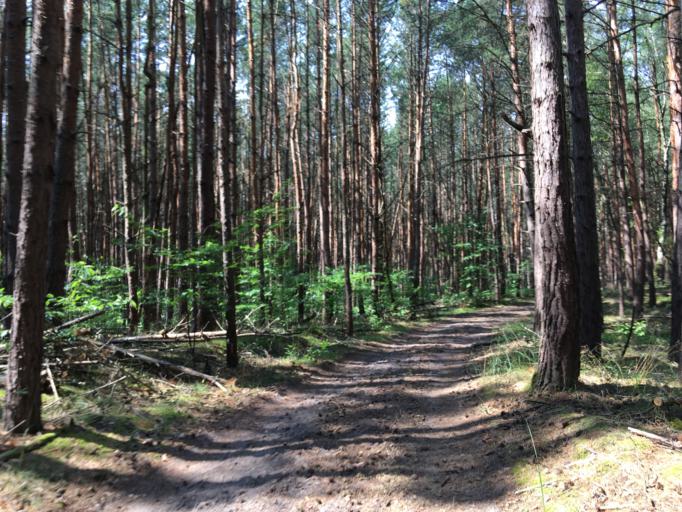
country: DE
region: Brandenburg
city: Glienicke
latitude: 52.6799
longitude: 13.3522
